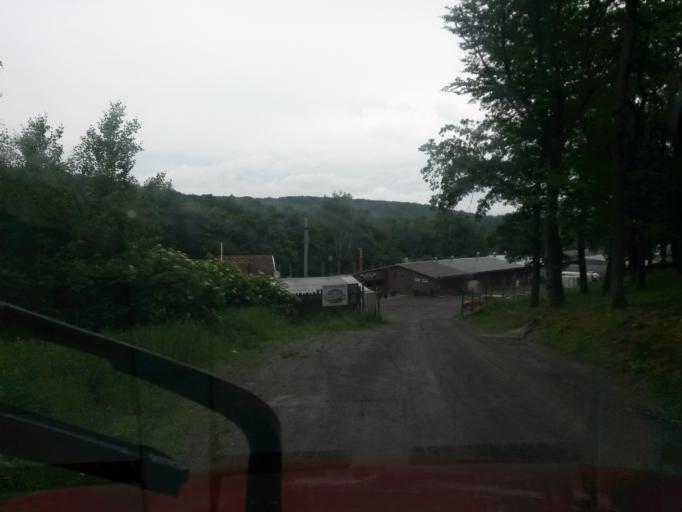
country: SK
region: Kosicky
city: Kosice
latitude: 48.7037
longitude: 21.1862
